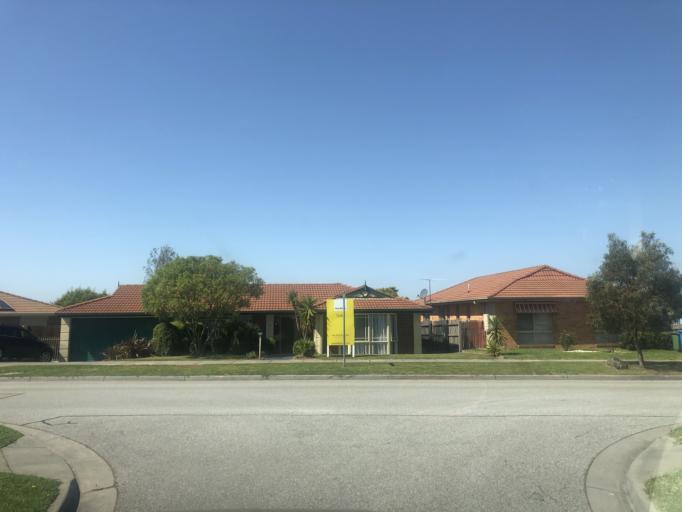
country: AU
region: Victoria
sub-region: Casey
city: Lynbrook
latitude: -38.0452
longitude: 145.2678
